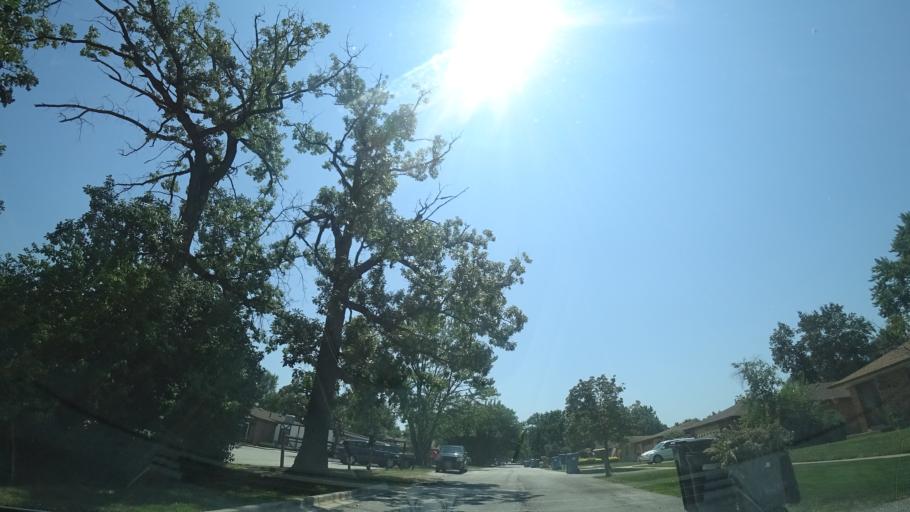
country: US
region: Illinois
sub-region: Cook County
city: Alsip
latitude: 41.6829
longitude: -87.7444
